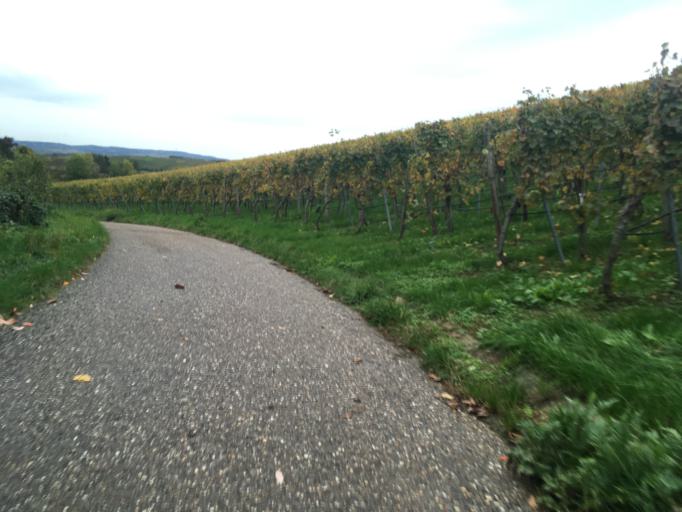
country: DE
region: Baden-Wuerttemberg
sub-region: Regierungsbezirk Stuttgart
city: Neckarwestheim
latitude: 49.0591
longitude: 9.1870
